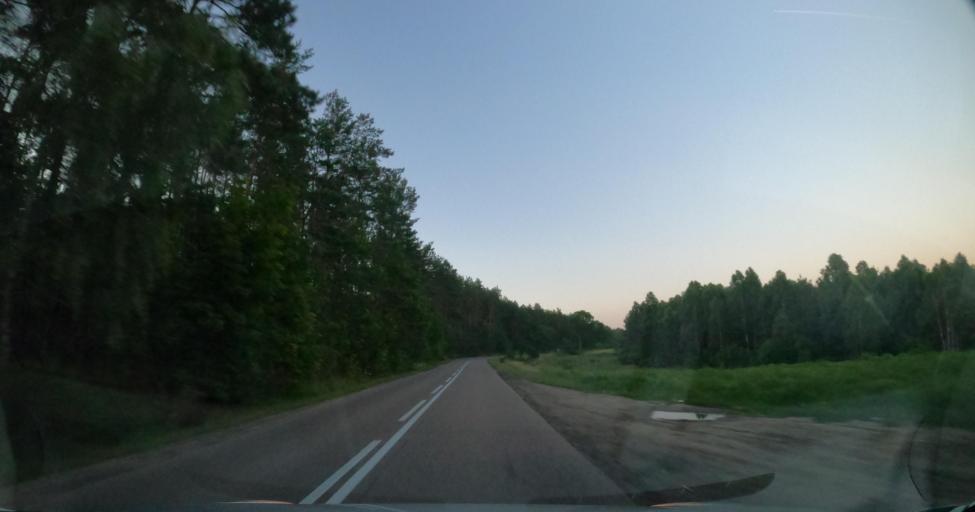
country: PL
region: Pomeranian Voivodeship
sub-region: Powiat wejherowski
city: Luzino
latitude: 54.4739
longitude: 18.0824
